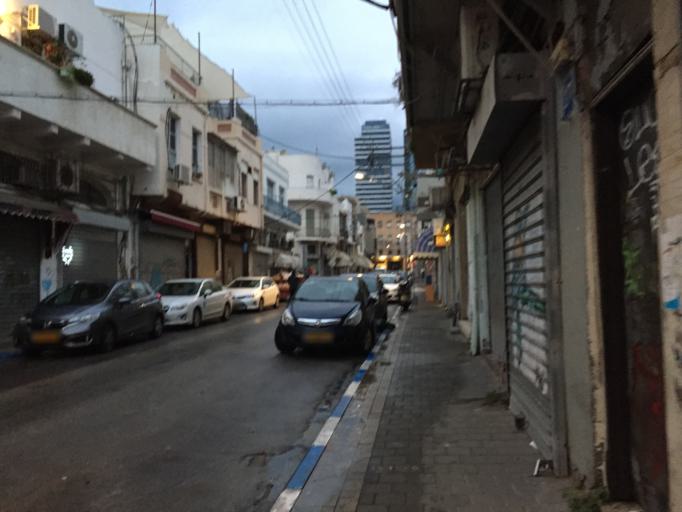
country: IL
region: Tel Aviv
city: Yafo
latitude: 32.0591
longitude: 34.7698
